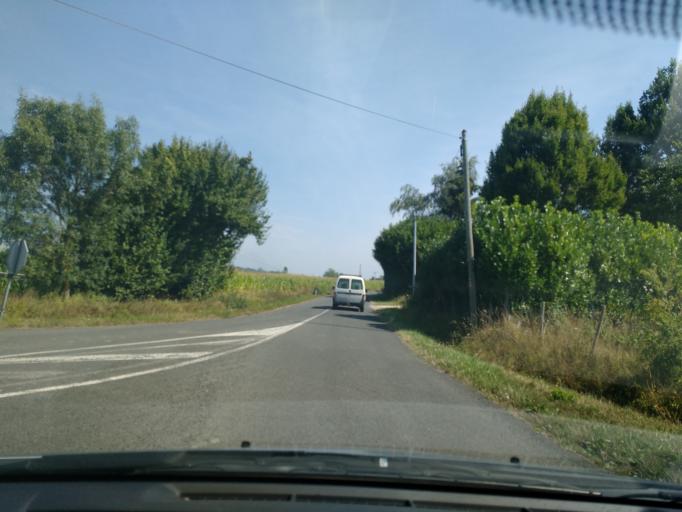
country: FR
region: Pays de la Loire
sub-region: Departement de Maine-et-Loire
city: Beaufort-en-Vallee
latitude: 47.4818
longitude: -0.2318
